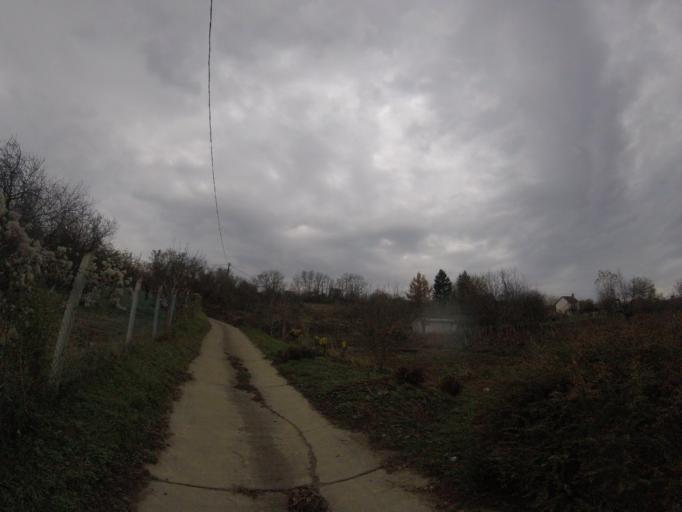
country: HU
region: Tolna
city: Szekszard
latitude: 46.3280
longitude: 18.6871
